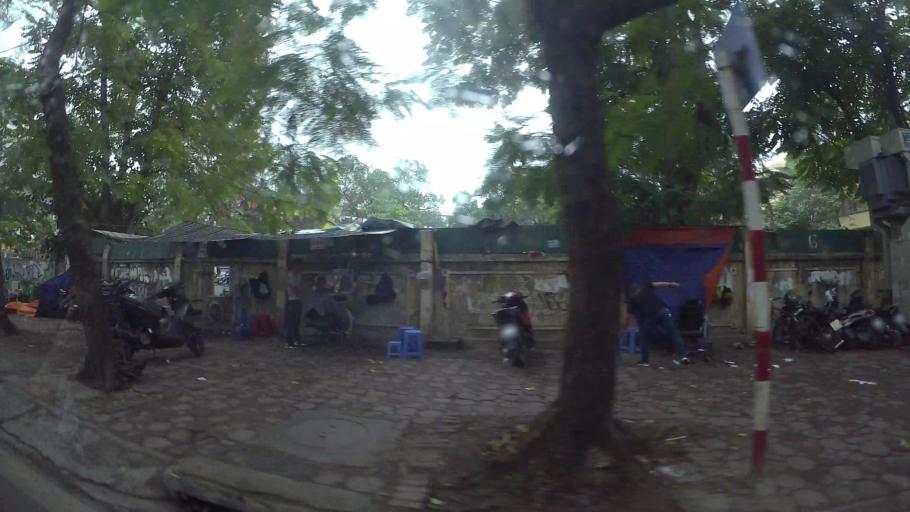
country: VN
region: Ha Noi
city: Dong Da
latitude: 21.0123
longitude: 105.8170
